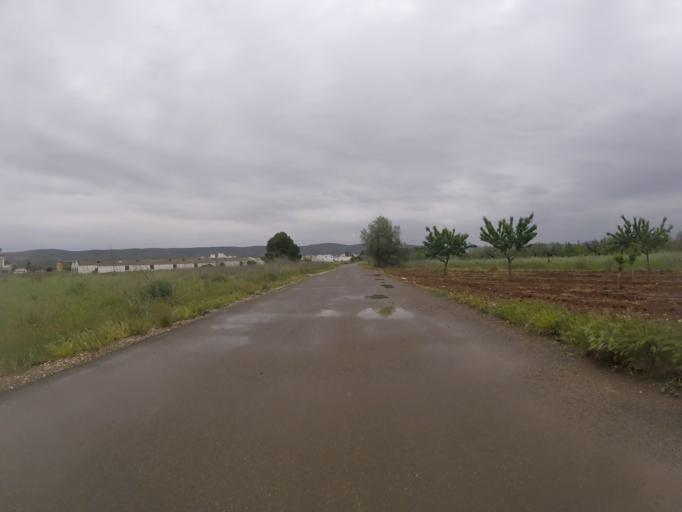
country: ES
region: Valencia
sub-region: Provincia de Castello
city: Alcala de Xivert
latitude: 40.2950
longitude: 0.2285
